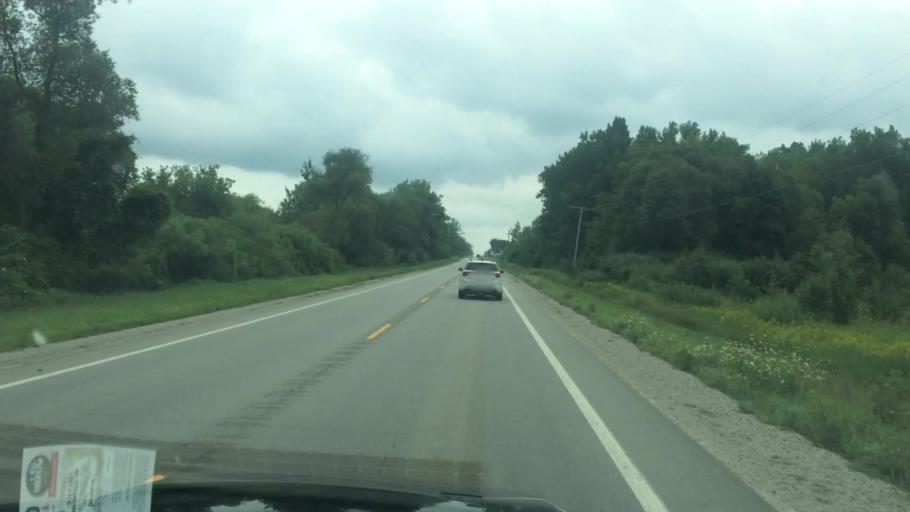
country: US
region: Michigan
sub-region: Tuscola County
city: Cass City
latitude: 43.5926
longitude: -83.0966
